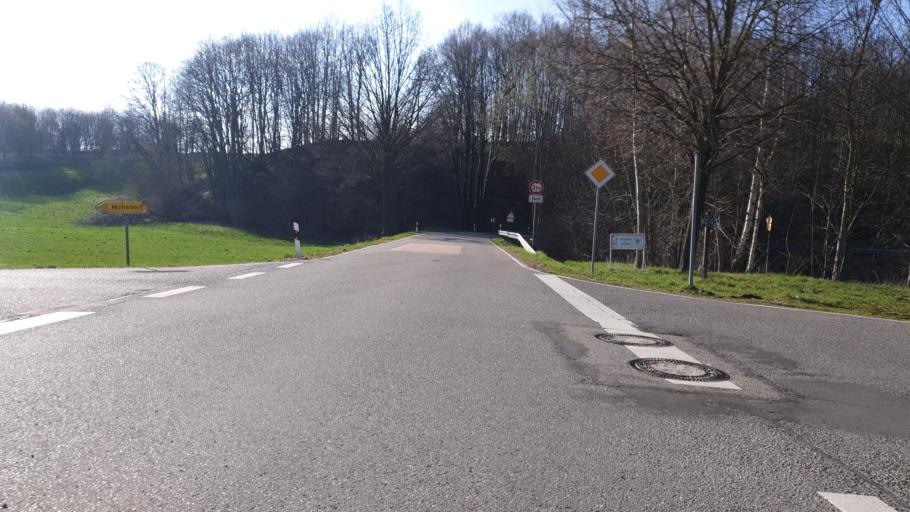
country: DE
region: Saxony
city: Taura
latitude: 50.9376
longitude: 12.8399
